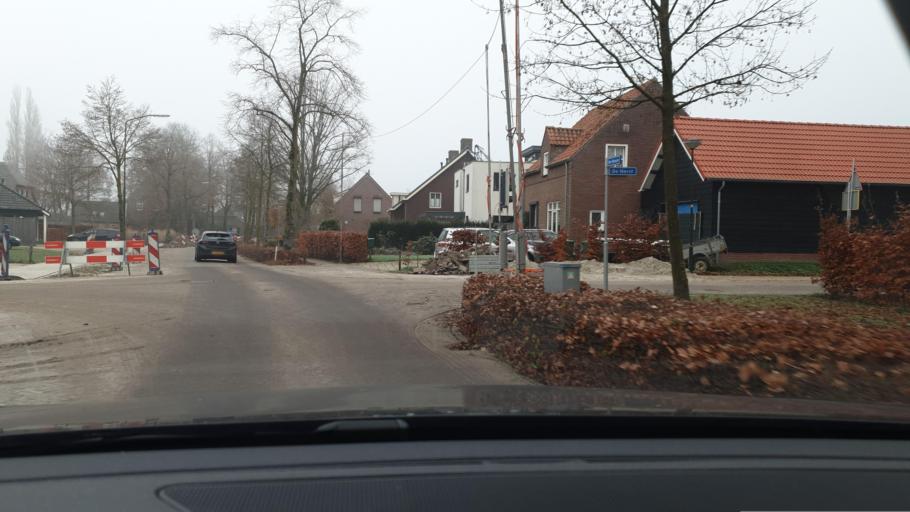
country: NL
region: North Brabant
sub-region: Gemeente Bladel en Netersel
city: Bladel
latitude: 51.4040
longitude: 5.2120
